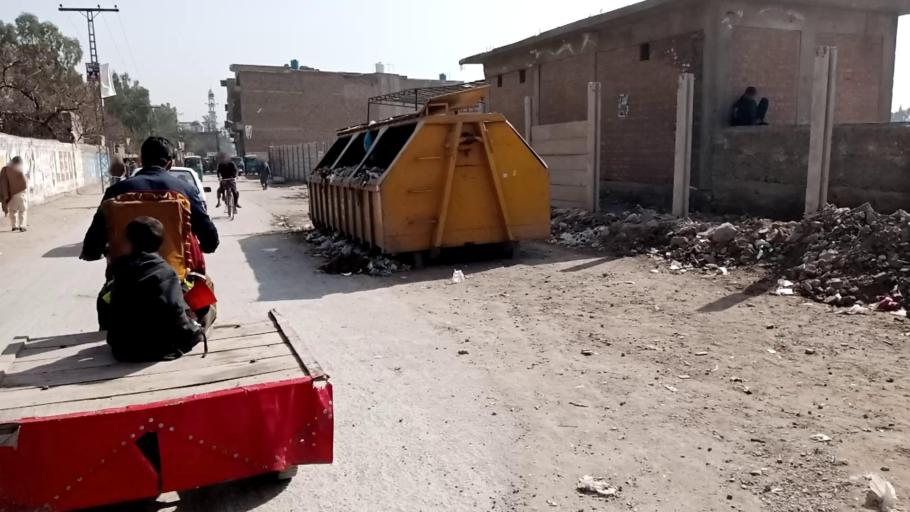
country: PK
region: Khyber Pakhtunkhwa
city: Peshawar
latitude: 33.9963
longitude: 71.5819
